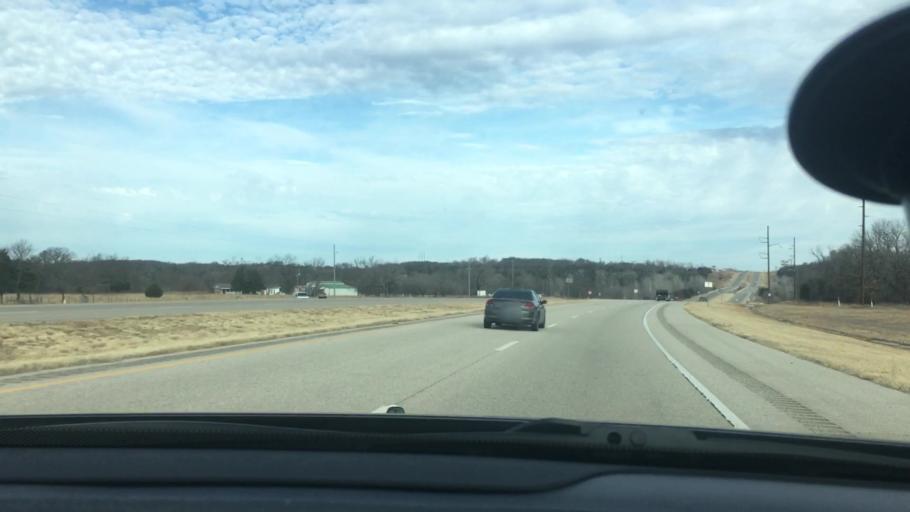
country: US
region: Oklahoma
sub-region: Pontotoc County
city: Byng
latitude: 34.9244
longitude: -96.6838
